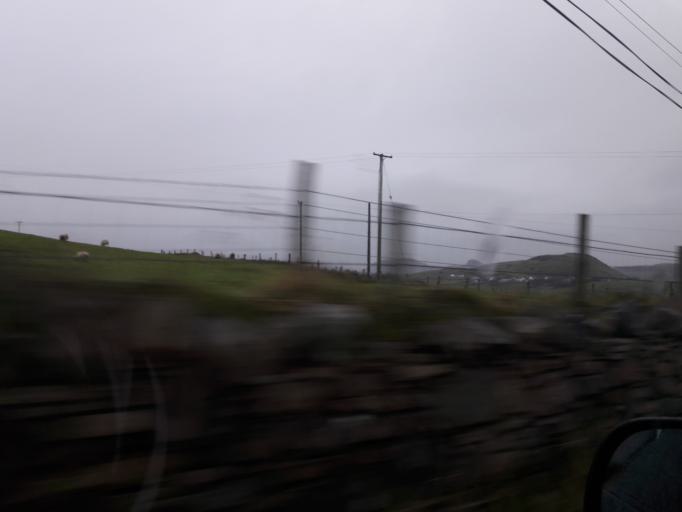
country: IE
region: Ulster
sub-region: County Donegal
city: Ramelton
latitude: 55.2611
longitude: -7.6671
